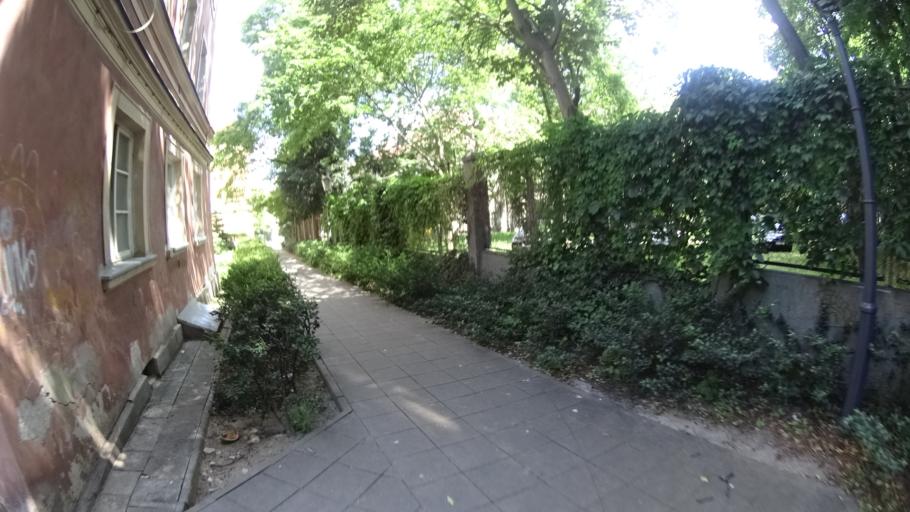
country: PL
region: Masovian Voivodeship
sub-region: Warszawa
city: Warsaw
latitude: 52.2524
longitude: 21.0089
